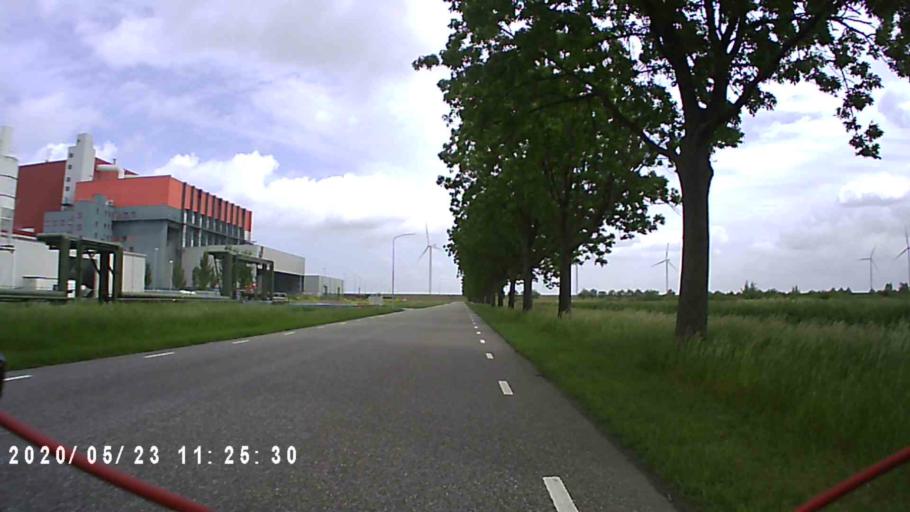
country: NL
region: Groningen
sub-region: Gemeente Delfzijl
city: Delfzijl
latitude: 53.3074
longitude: 6.9894
